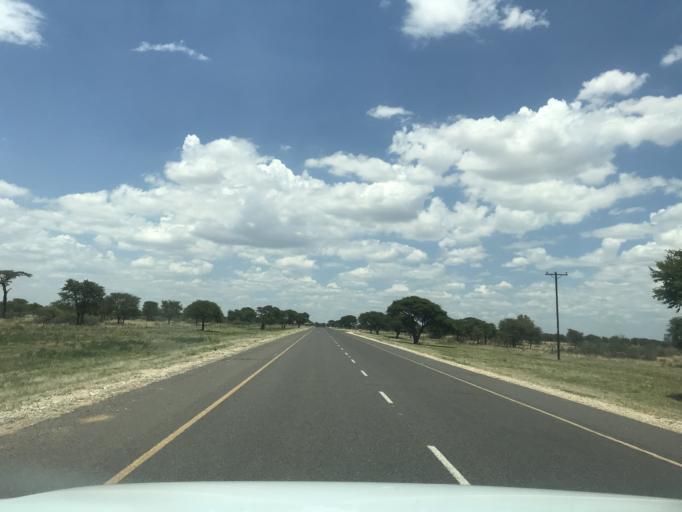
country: BW
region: South East
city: Janeng
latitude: -25.6385
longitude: 25.1519
